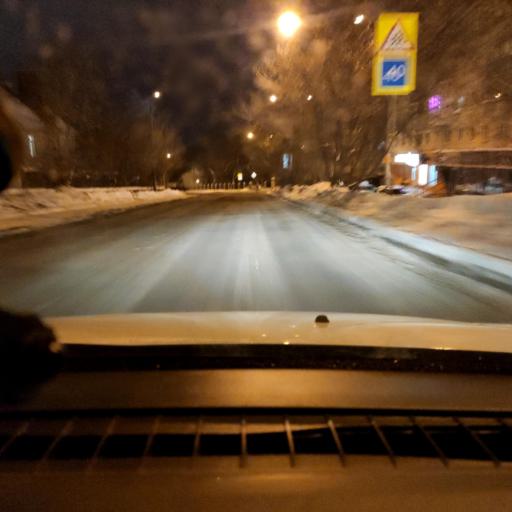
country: RU
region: Samara
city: Volzhskiy
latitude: 53.3890
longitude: 50.1695
